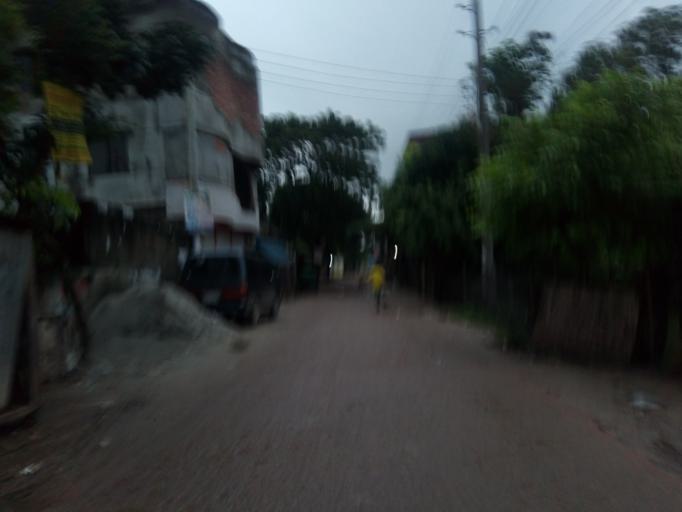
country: BD
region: Dhaka
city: Tungi
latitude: 23.8540
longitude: 90.4314
